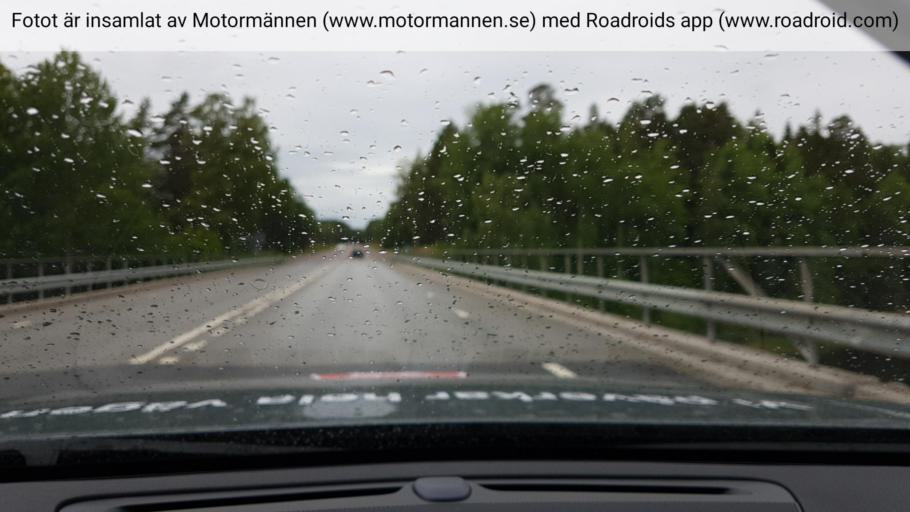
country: SE
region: Uppsala
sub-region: Alvkarleby Kommun
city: AElvkarleby
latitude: 60.6031
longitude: 17.4496
